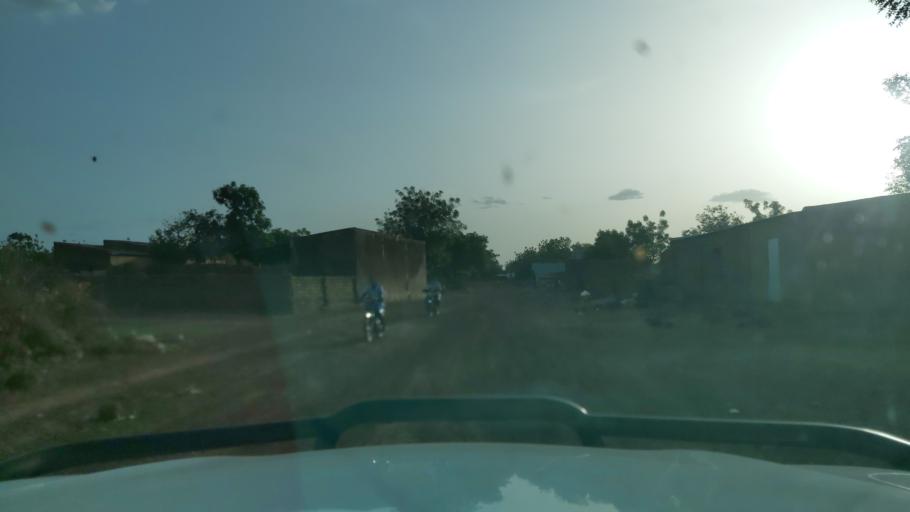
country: ML
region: Koulikoro
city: Kolokani
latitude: 13.2033
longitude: -7.9297
